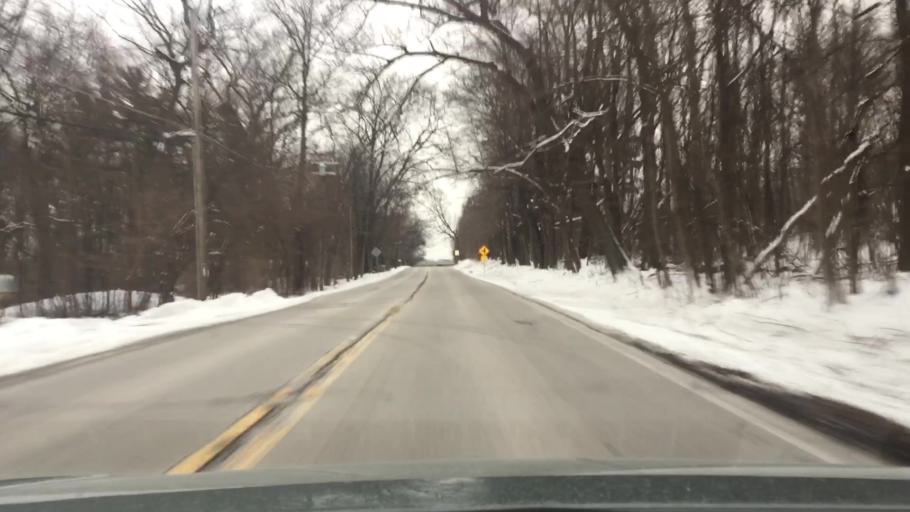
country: US
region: Wisconsin
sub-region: Waukesha County
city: Pewaukee
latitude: 43.0491
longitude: -88.3129
